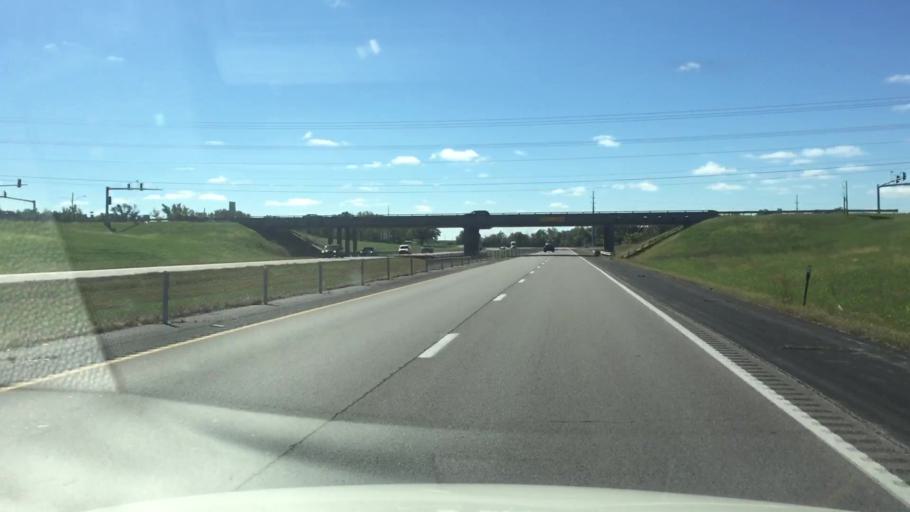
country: US
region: Missouri
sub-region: Boone County
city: Columbia
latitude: 38.9141
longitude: -92.2939
